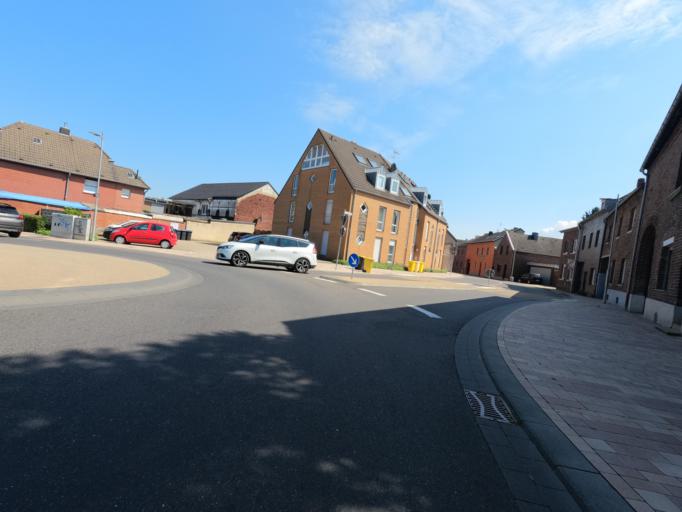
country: DE
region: North Rhine-Westphalia
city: Baesweiler
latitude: 50.9219
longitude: 6.2022
